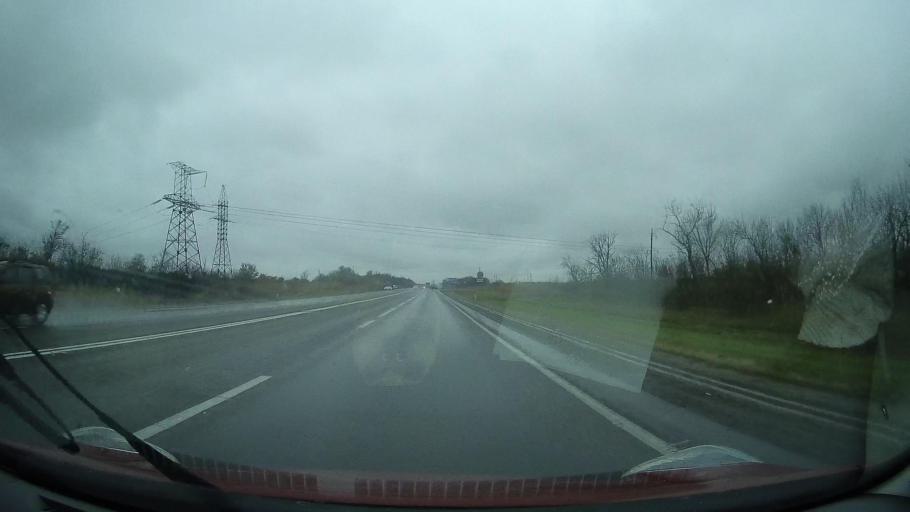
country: RU
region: Stavropol'skiy
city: Nevinnomyssk
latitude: 44.6339
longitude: 42.0087
